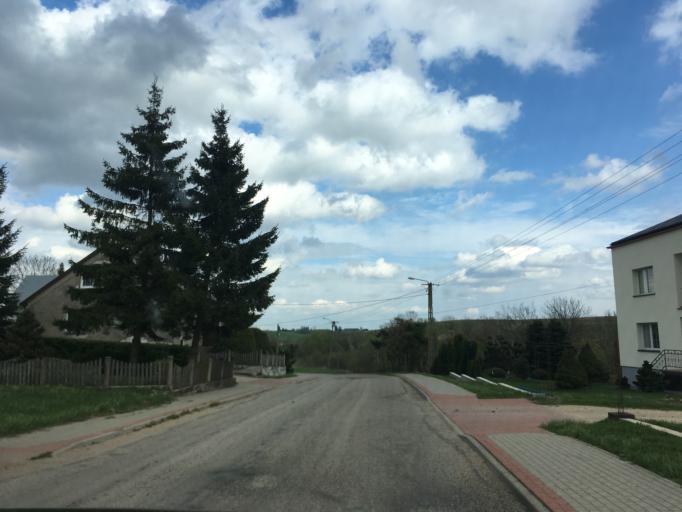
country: PL
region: Podlasie
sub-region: Suwalki
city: Suwalki
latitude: 54.3680
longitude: 22.8738
